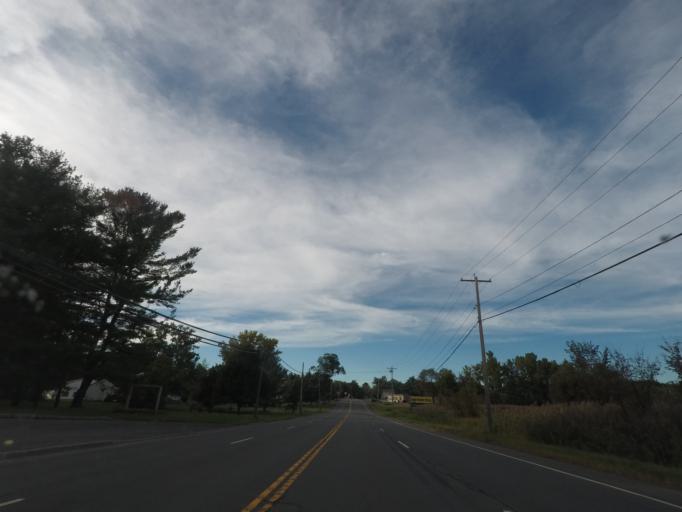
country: US
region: New York
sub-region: Rensselaer County
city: East Greenbush
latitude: 42.5717
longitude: -73.6869
